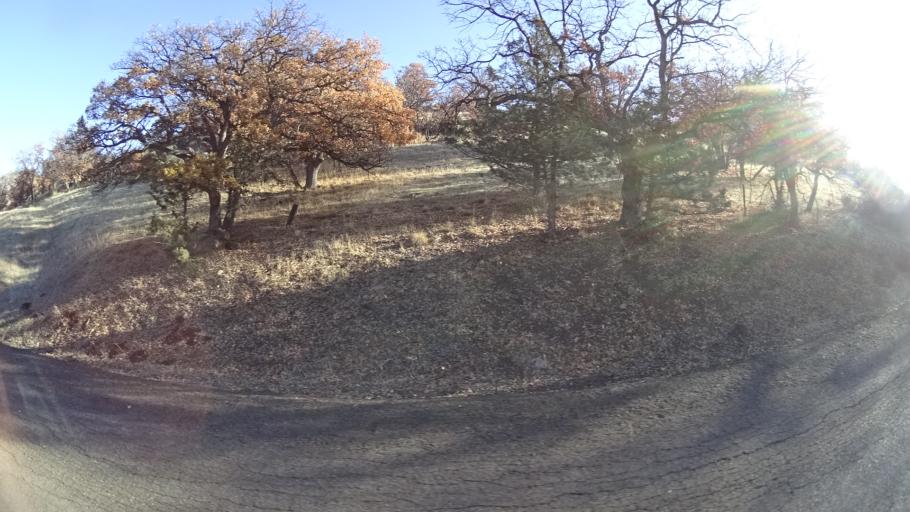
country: US
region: California
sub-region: Siskiyou County
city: Montague
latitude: 41.8910
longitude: -122.4974
